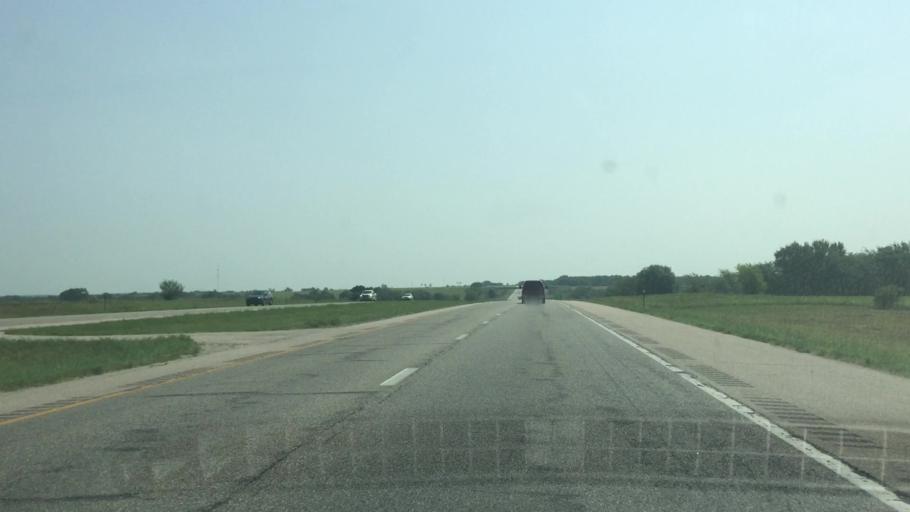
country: US
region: Kansas
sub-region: Osage County
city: Lyndon
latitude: 38.4264
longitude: -95.7615
